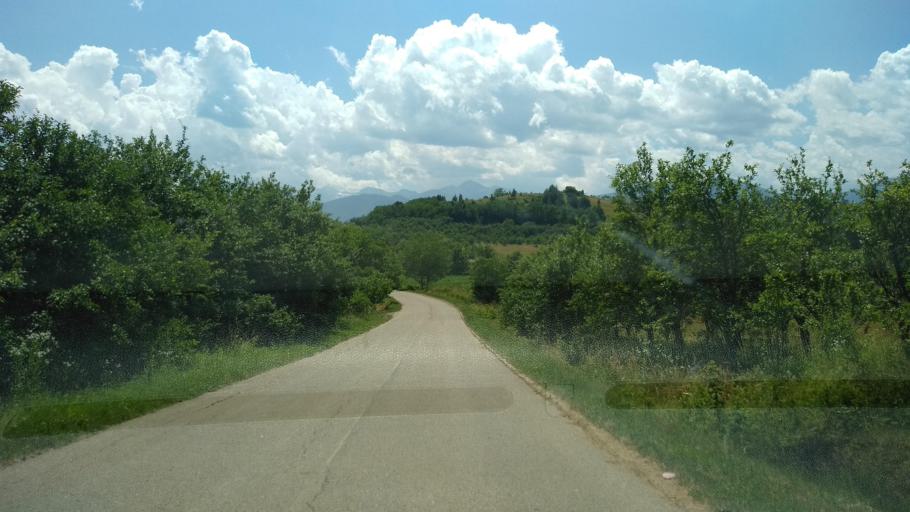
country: RO
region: Hunedoara
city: Densus
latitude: 45.5591
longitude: 22.8186
